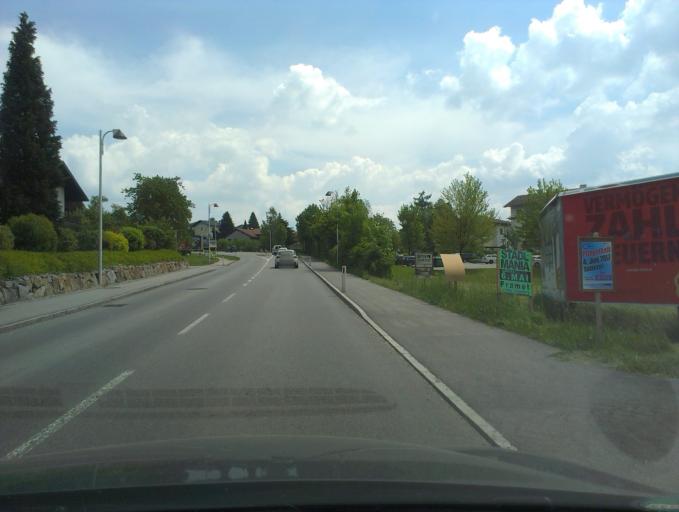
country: AT
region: Upper Austria
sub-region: Politischer Bezirk Ried im Innkreis
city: Ried im Innkreis
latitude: 48.2067
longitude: 13.4388
